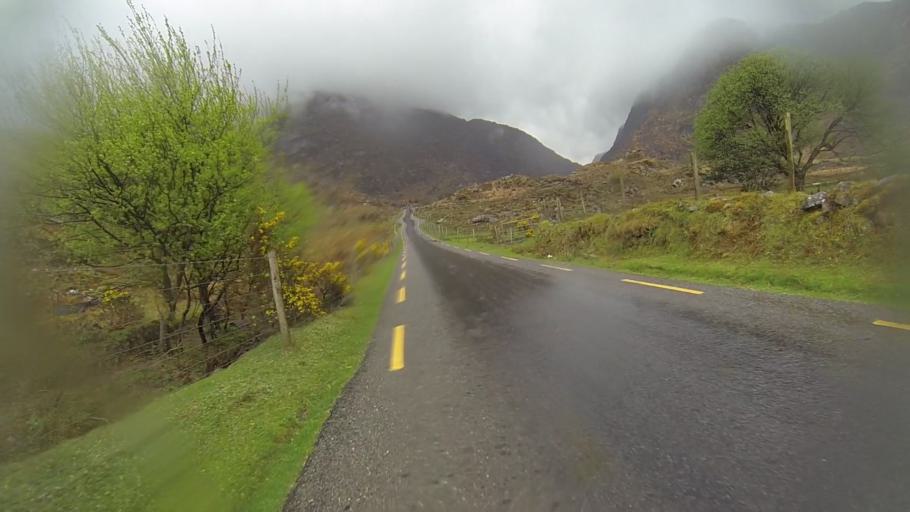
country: IE
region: Munster
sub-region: Ciarrai
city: Cill Airne
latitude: 52.0210
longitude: -9.6365
